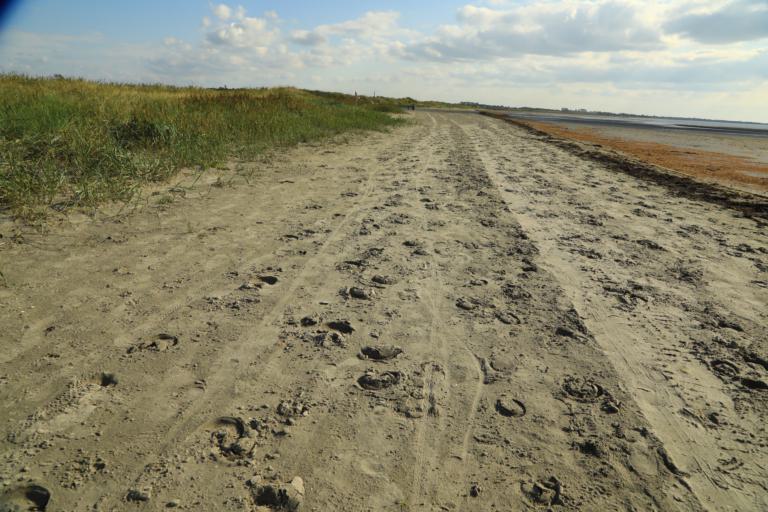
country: SE
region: Halland
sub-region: Varbergs Kommun
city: Tvaaker
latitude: 57.0087
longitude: 12.3466
